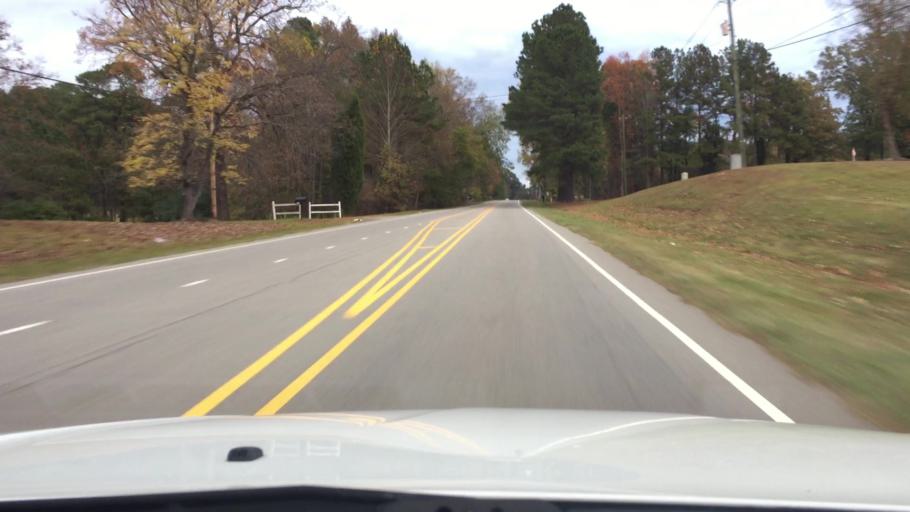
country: US
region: North Carolina
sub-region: Chatham County
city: Farmville
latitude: 35.5570
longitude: -79.1847
